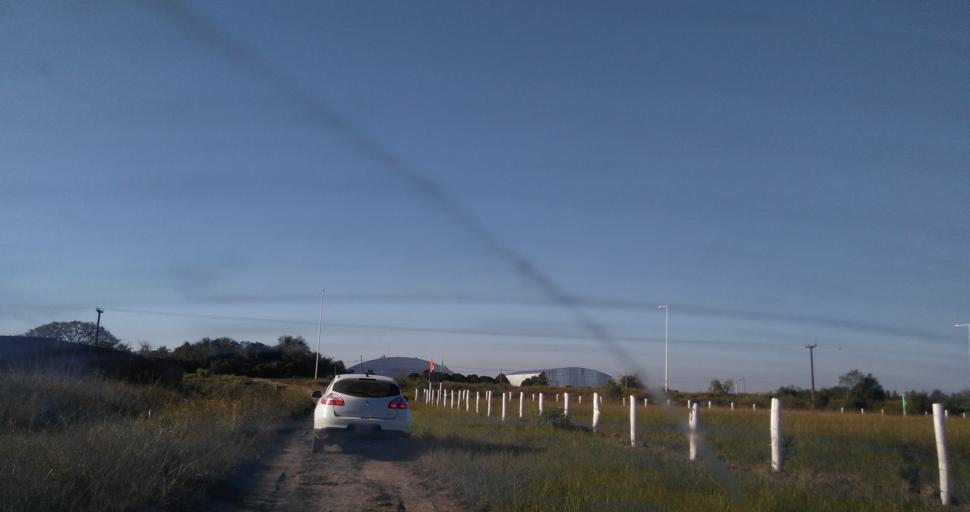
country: AR
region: Chaco
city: Fontana
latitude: -27.4626
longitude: -59.0437
